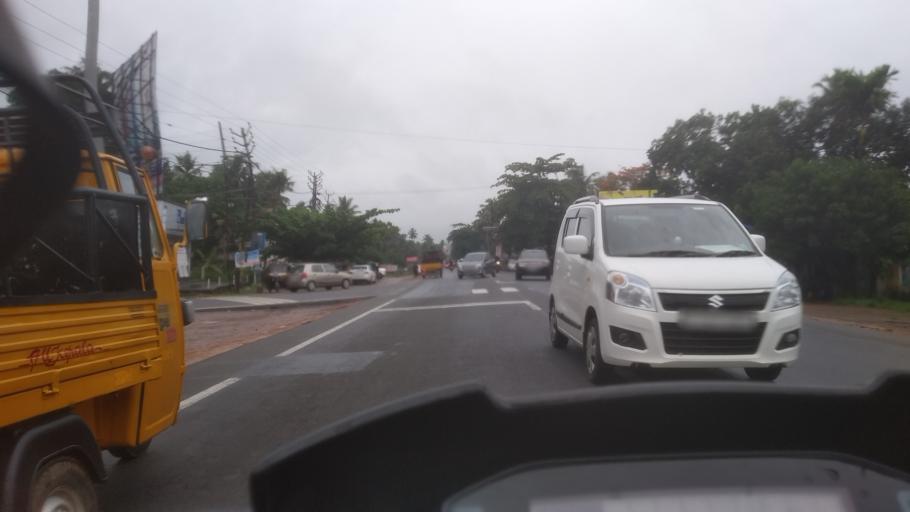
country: IN
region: Kerala
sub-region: Alappuzha
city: Kayankulam
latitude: 9.1611
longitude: 76.5067
